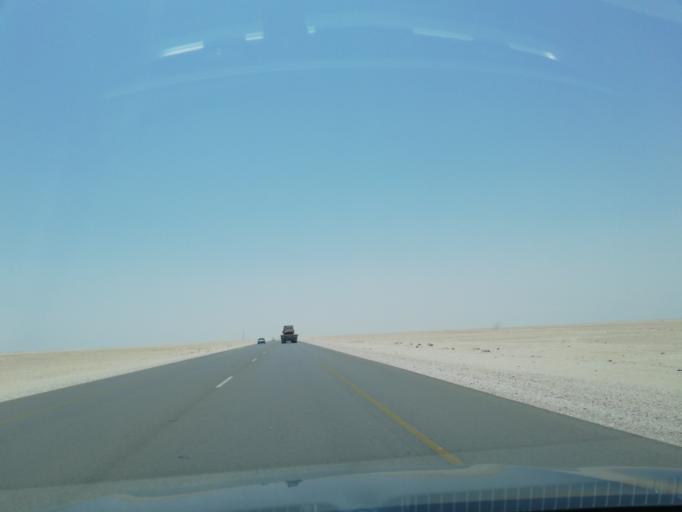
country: OM
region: Al Wusta
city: Hayma'
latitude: 20.1465
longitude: 56.5051
